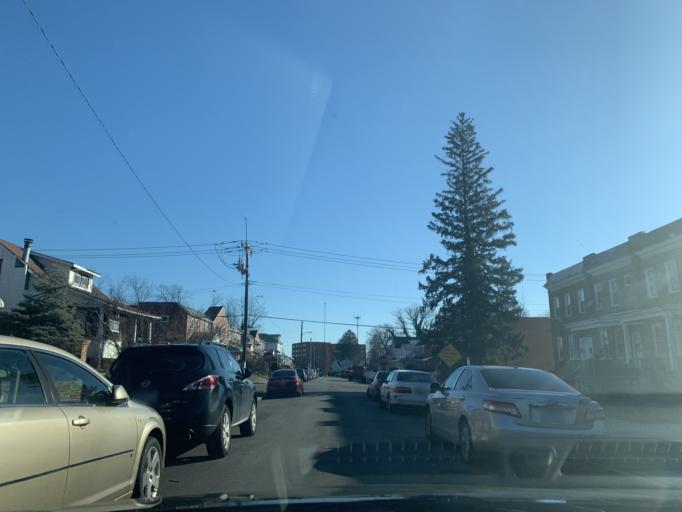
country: US
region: Maryland
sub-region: Baltimore County
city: Lochearn
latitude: 39.3345
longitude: -76.6794
